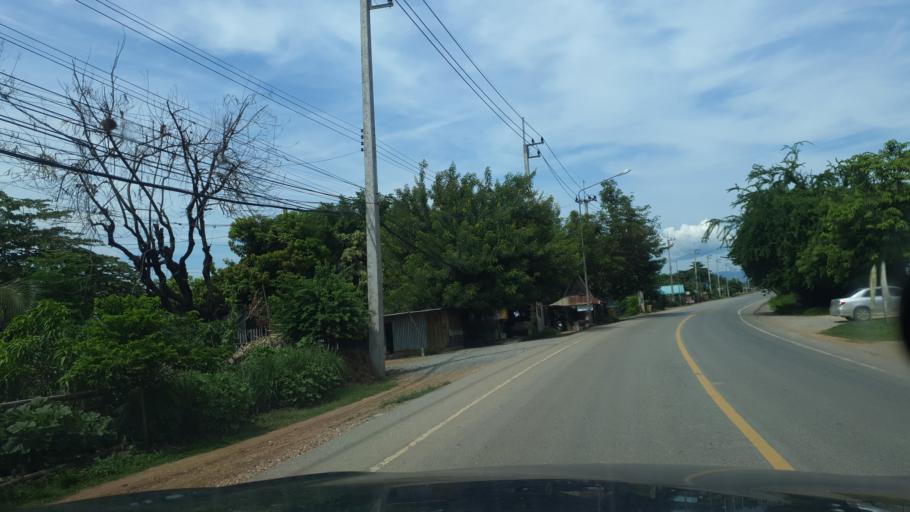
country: TH
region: Sukhothai
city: Sukhothai
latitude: 17.0608
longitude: 99.8290
